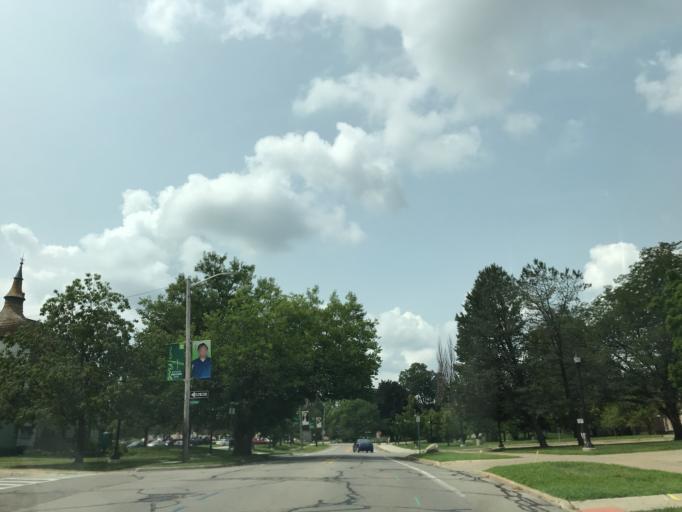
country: US
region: Michigan
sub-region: Washtenaw County
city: Ypsilanti
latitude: 42.2479
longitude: -83.6203
